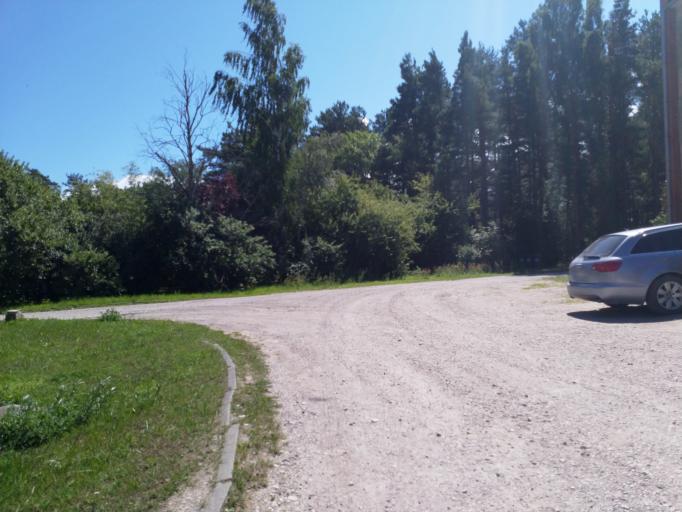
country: LV
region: Dundaga
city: Dundaga
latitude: 57.7361
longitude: 22.5822
